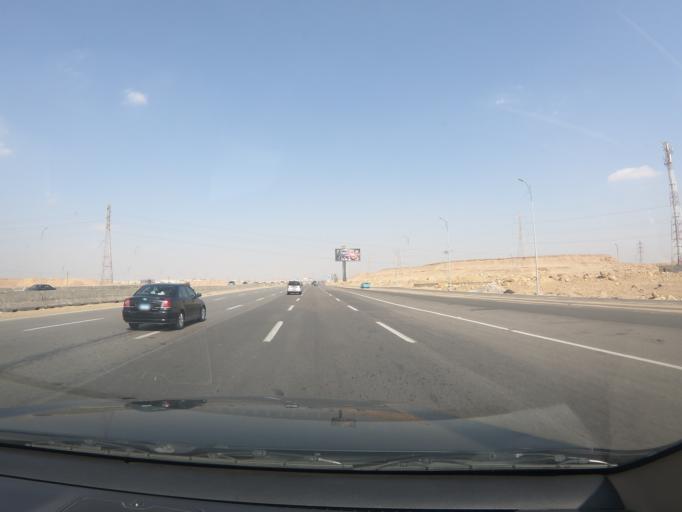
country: EG
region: Muhafazat al Qalyubiyah
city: Al Khankah
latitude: 30.1031
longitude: 31.5893
